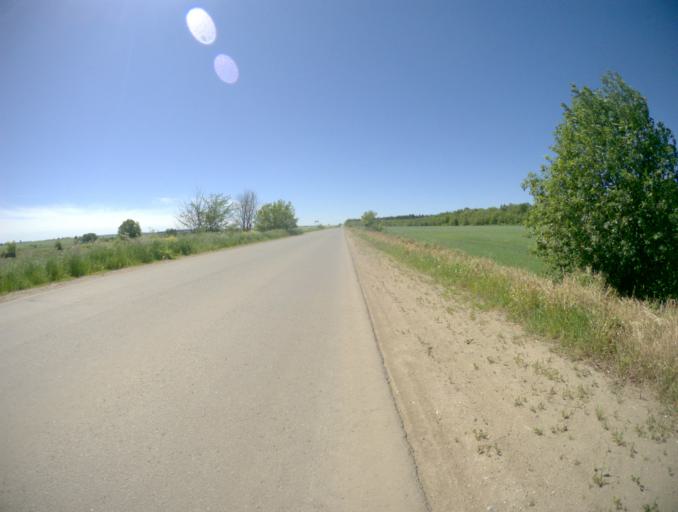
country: RU
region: Ivanovo
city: Gavrilov Posad
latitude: 56.5653
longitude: 40.0532
